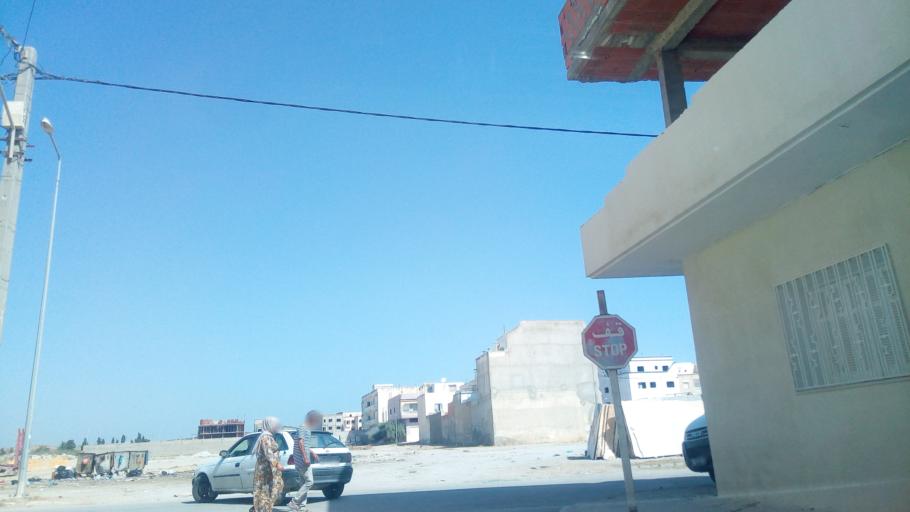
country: TN
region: Nabul
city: Dar Chabanne
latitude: 36.4679
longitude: 10.7414
